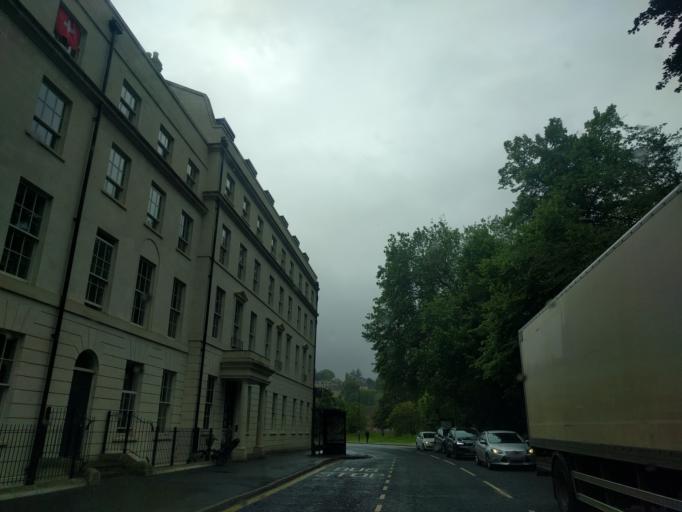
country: GB
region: England
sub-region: Bath and North East Somerset
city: Bath
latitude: 51.3807
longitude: -2.3663
